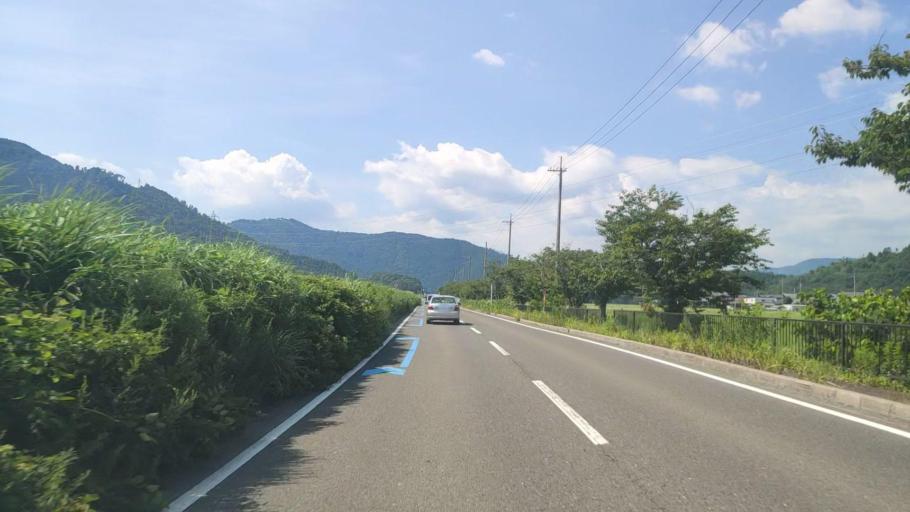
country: JP
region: Shiga Prefecture
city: Nagahama
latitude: 35.4831
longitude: 136.2093
